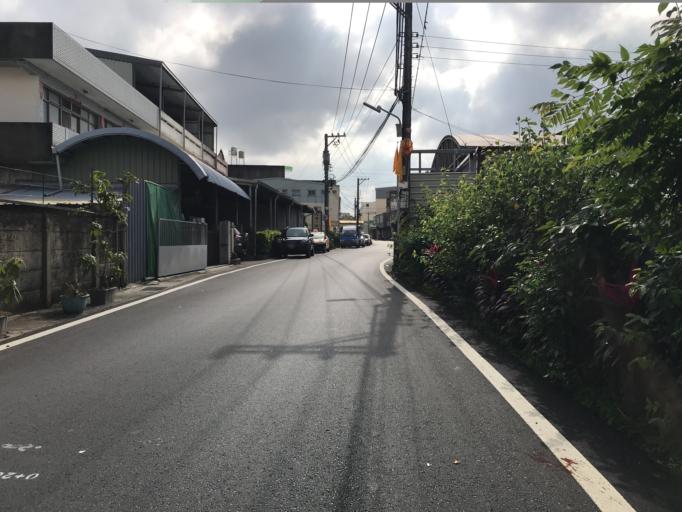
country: TW
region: Taiwan
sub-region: Hsinchu
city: Zhubei
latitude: 24.8090
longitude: 121.0048
